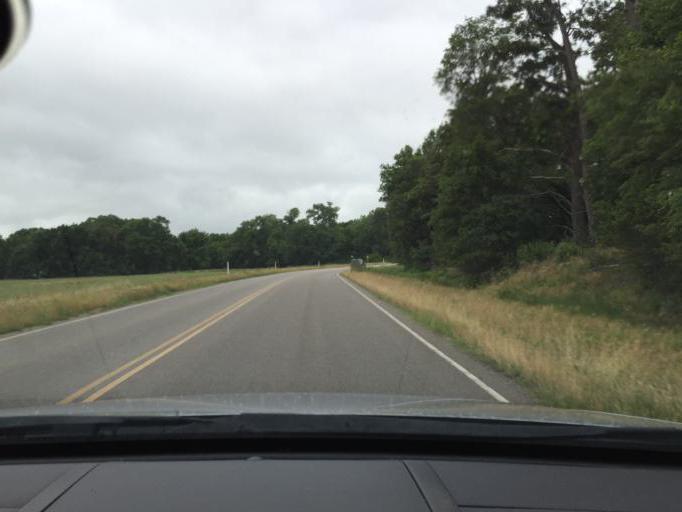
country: US
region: Kansas
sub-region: Reno County
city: Buhler
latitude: 38.1447
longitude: -97.8267
